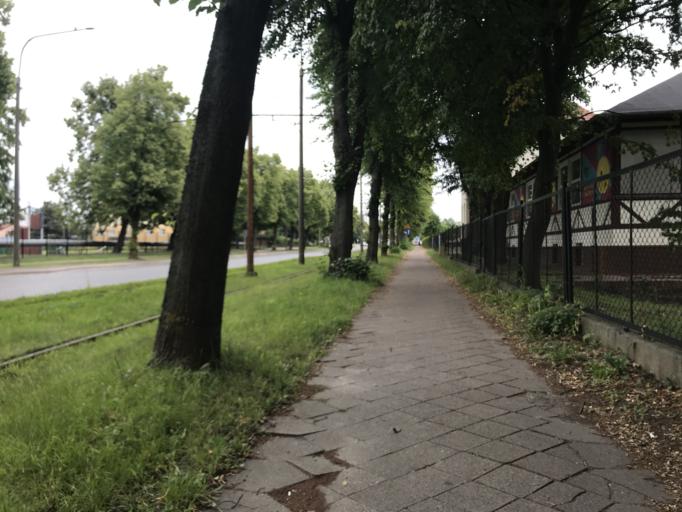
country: PL
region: Warmian-Masurian Voivodeship
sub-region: Powiat elblaski
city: Elblag
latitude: 54.1765
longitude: 19.4210
